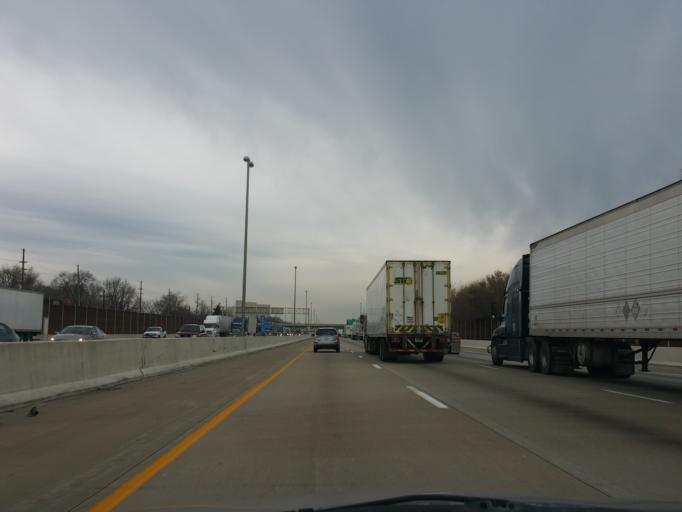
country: US
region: Indiana
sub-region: Lake County
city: Hammond
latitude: 41.5743
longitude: -87.4939
